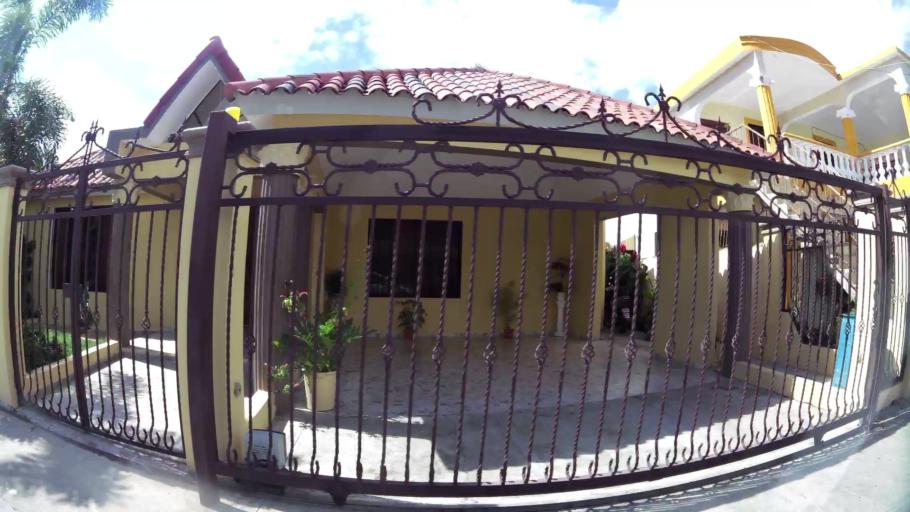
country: DO
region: Santiago
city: Santiago de los Caballeros
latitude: 19.4707
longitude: -70.6998
